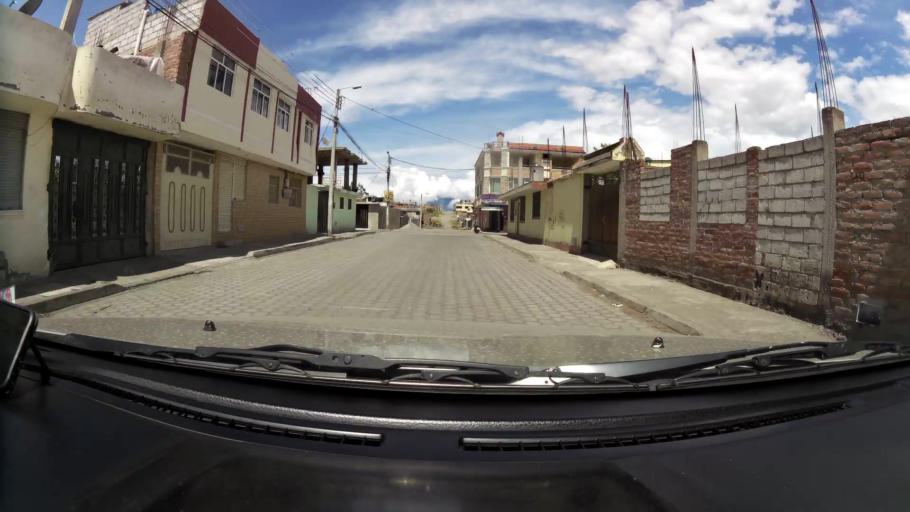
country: EC
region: Chimborazo
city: Riobamba
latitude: -1.6601
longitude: -78.6379
